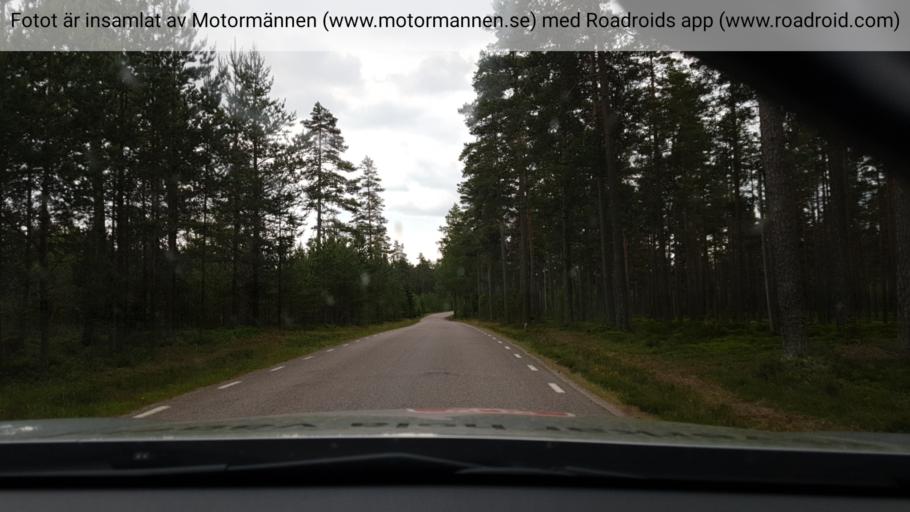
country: SE
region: Joenkoeping
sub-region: Habo Kommun
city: Habo
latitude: 58.0413
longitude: 14.0219
